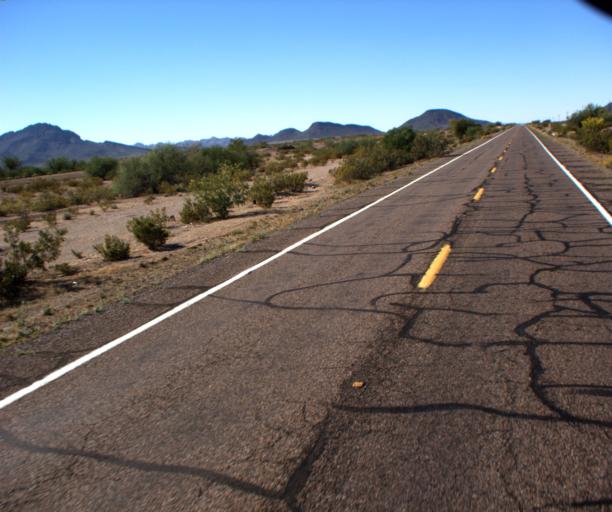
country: US
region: Arizona
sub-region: Maricopa County
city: Gila Bend
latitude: 32.8036
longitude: -112.7976
